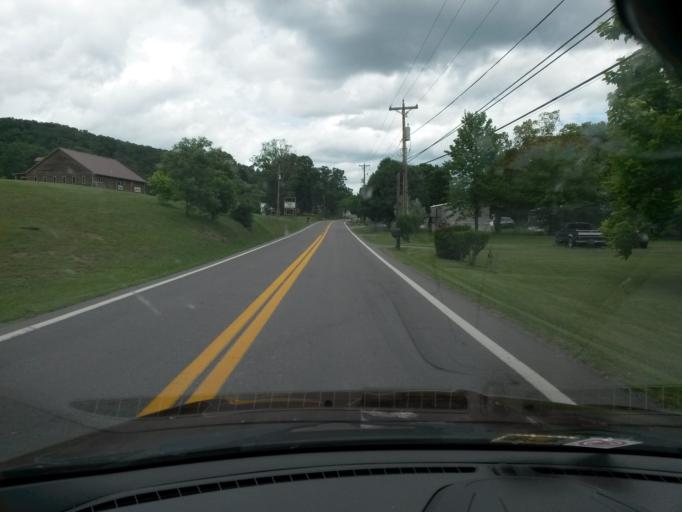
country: US
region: Virginia
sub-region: Giles County
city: Pearisburg
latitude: 37.4086
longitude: -80.7559
